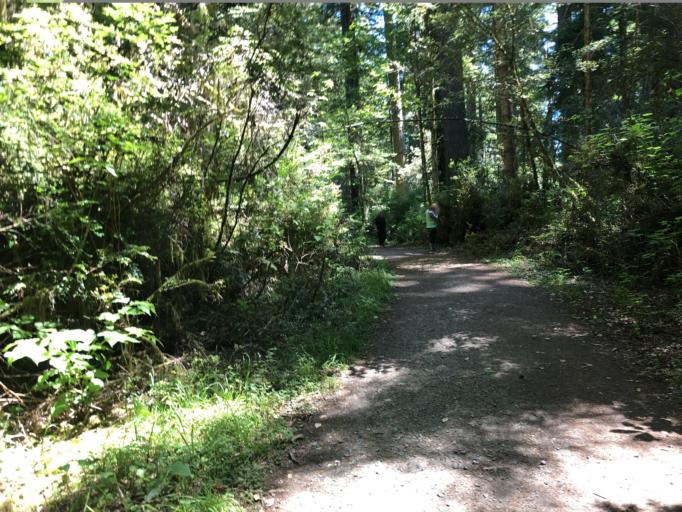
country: US
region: California
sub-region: Humboldt County
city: Westhaven-Moonstone
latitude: 41.3076
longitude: -124.0237
